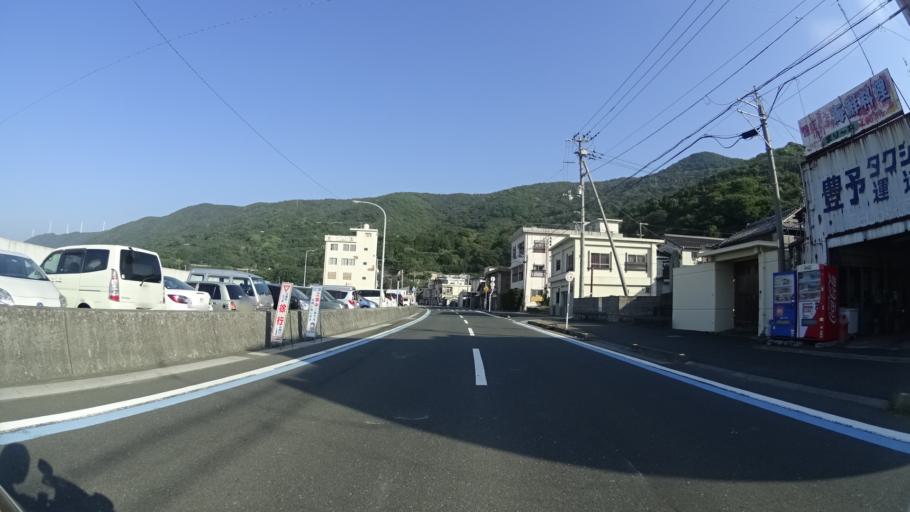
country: JP
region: Ehime
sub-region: Nishiuwa-gun
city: Ikata-cho
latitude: 33.3900
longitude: 132.1200
